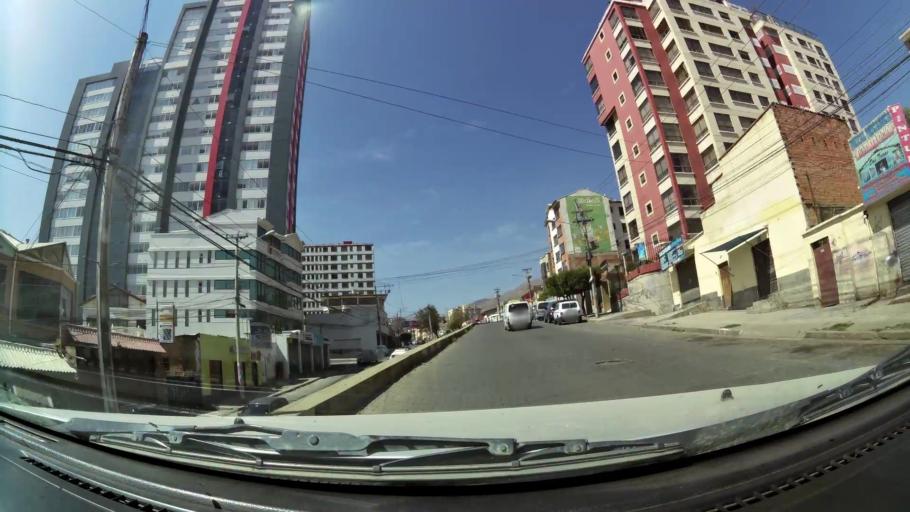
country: BO
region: La Paz
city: La Paz
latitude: -16.5404
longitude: -68.0694
